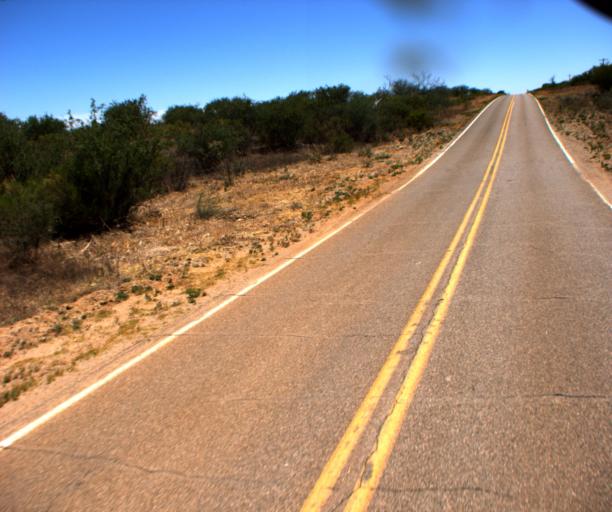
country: US
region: Arizona
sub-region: Pima County
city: Arivaca Junction
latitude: 31.6398
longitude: -111.5026
